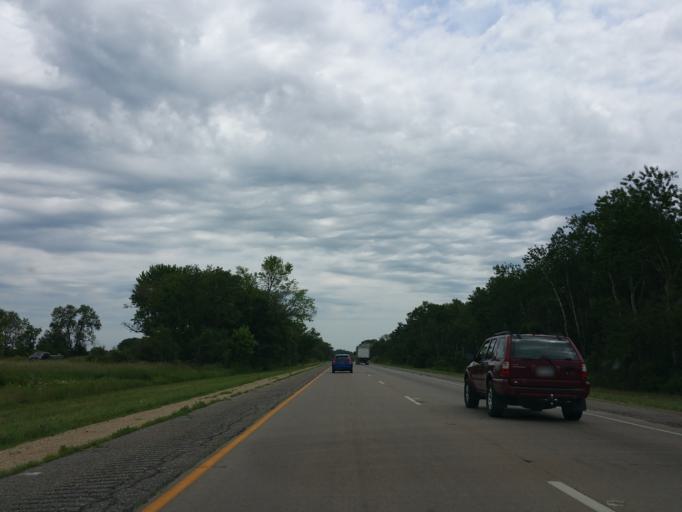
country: US
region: Wisconsin
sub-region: Juneau County
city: Mauston
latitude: 43.7796
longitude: -90.0300
